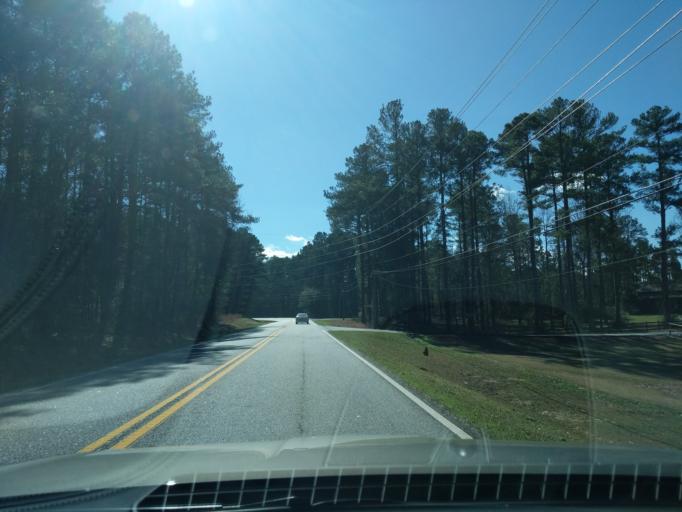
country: US
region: Georgia
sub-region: Columbia County
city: Evans
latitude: 33.5467
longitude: -82.1655
